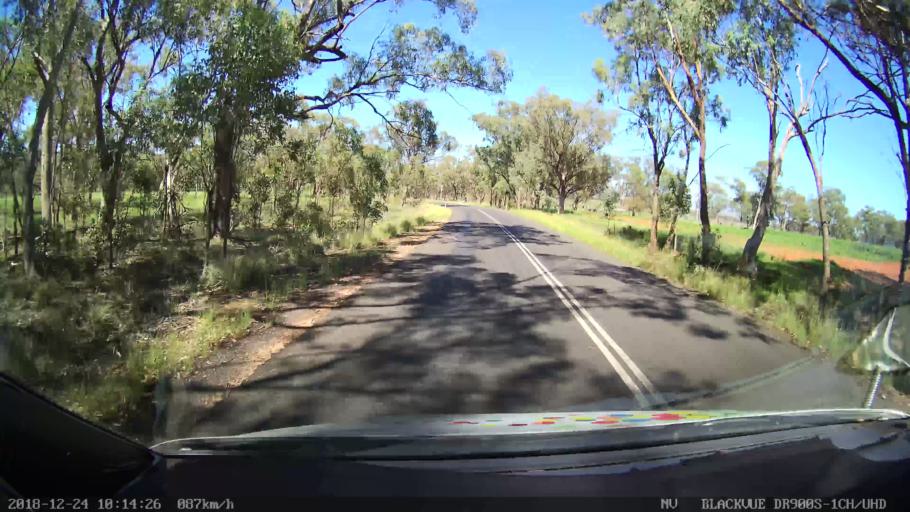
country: AU
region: New South Wales
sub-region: Liverpool Plains
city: Quirindi
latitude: -31.6975
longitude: 150.6281
